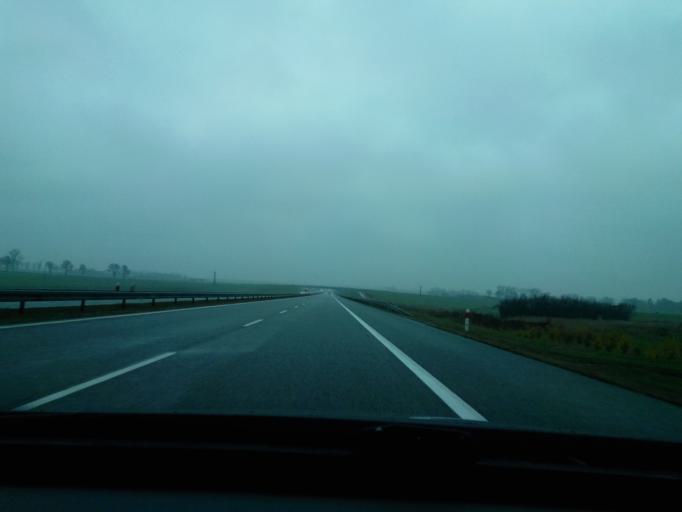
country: PL
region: Pomeranian Voivodeship
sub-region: Powiat tczewski
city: Tczew
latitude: 54.0867
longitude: 18.6917
